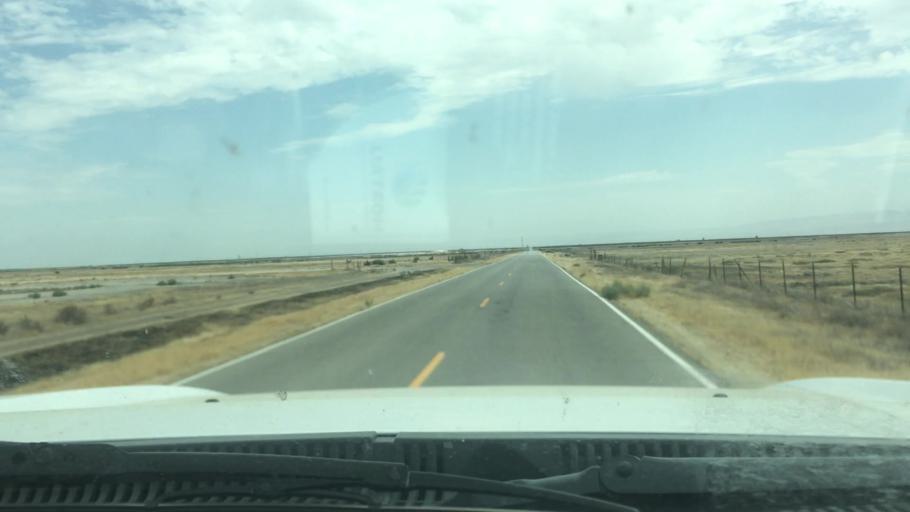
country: US
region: California
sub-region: Kern County
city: Lost Hills
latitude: 35.6603
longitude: -119.5800
